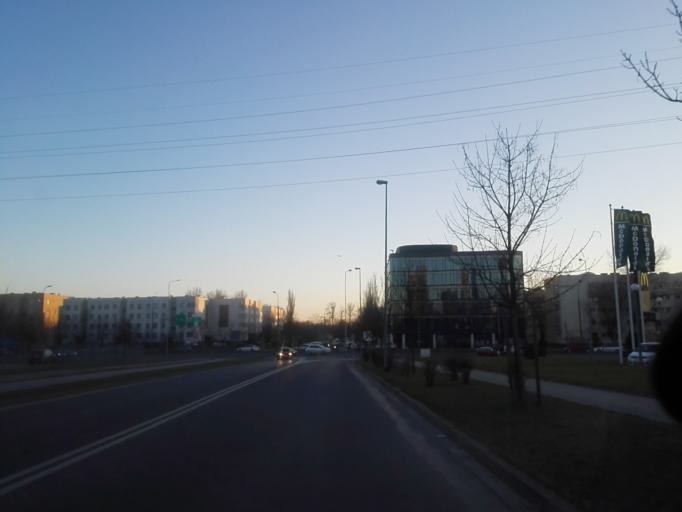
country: PL
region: Masovian Voivodeship
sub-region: Warszawa
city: Mokotow
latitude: 52.1704
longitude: 21.0104
